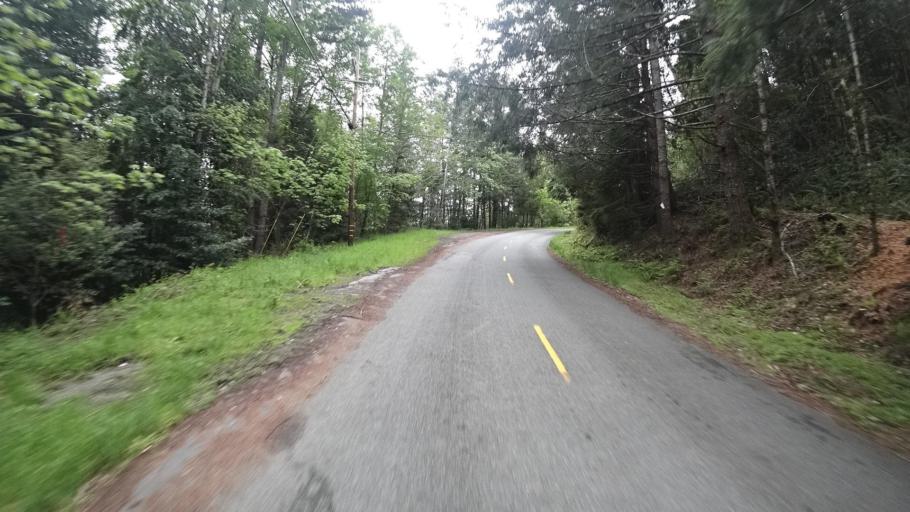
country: US
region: California
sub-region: Humboldt County
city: Blue Lake
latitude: 40.9455
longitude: -123.8425
